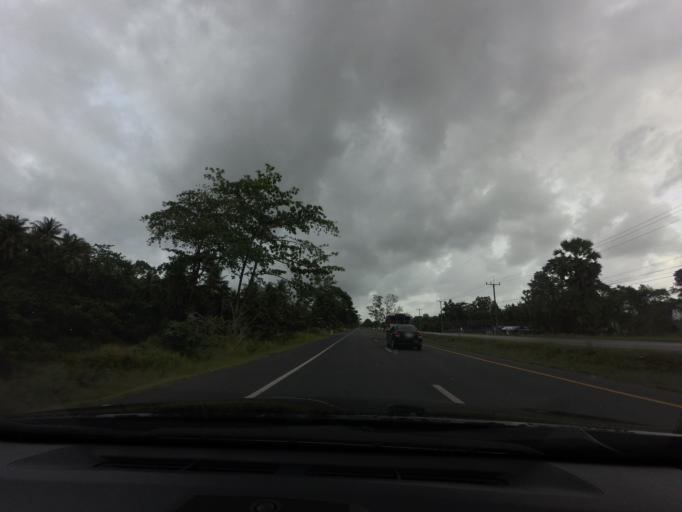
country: TH
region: Pattani
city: Mayo
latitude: 6.7700
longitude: 101.4651
